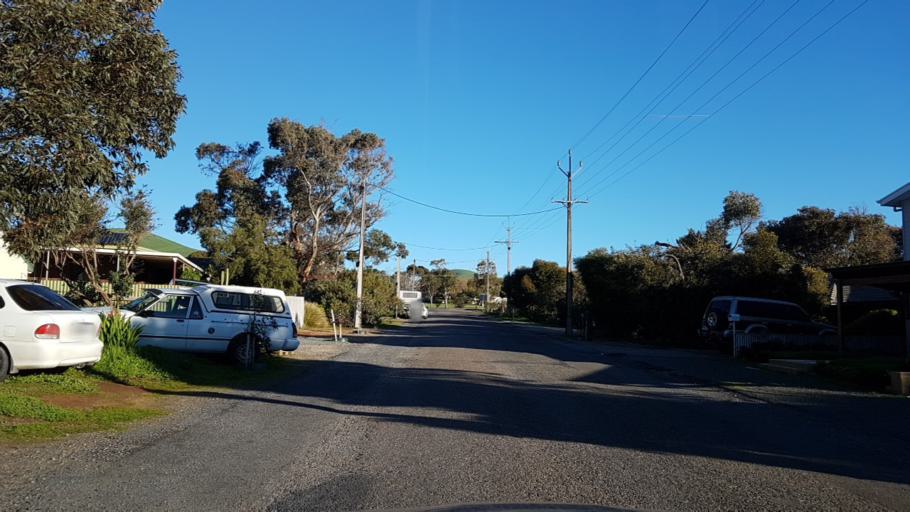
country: AU
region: South Australia
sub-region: Onkaparinga
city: Port Willunga
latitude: -35.3379
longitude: 138.4496
